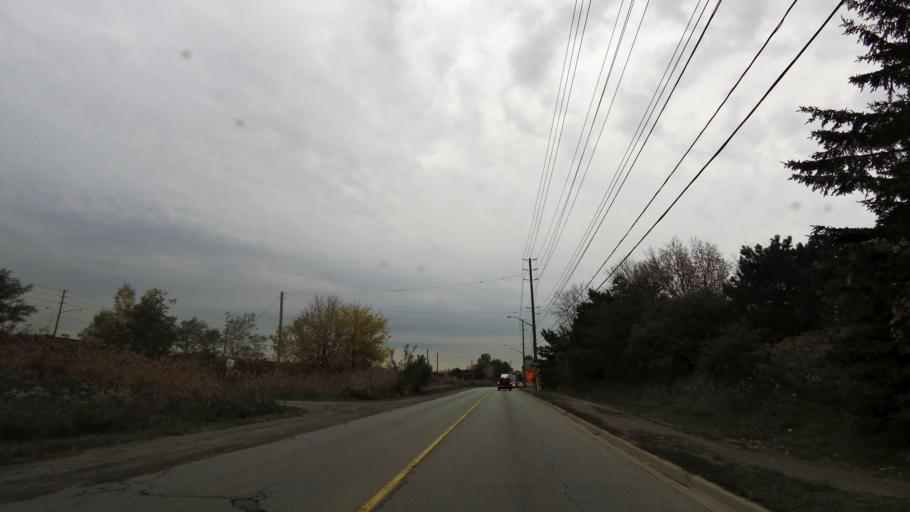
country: CA
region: Ontario
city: Oakville
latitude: 43.4695
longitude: -79.6693
